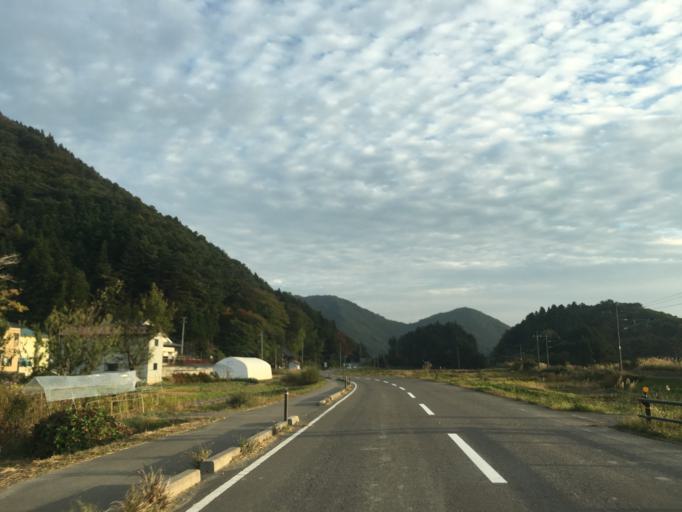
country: JP
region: Fukushima
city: Inawashiro
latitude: 37.5097
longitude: 140.1454
